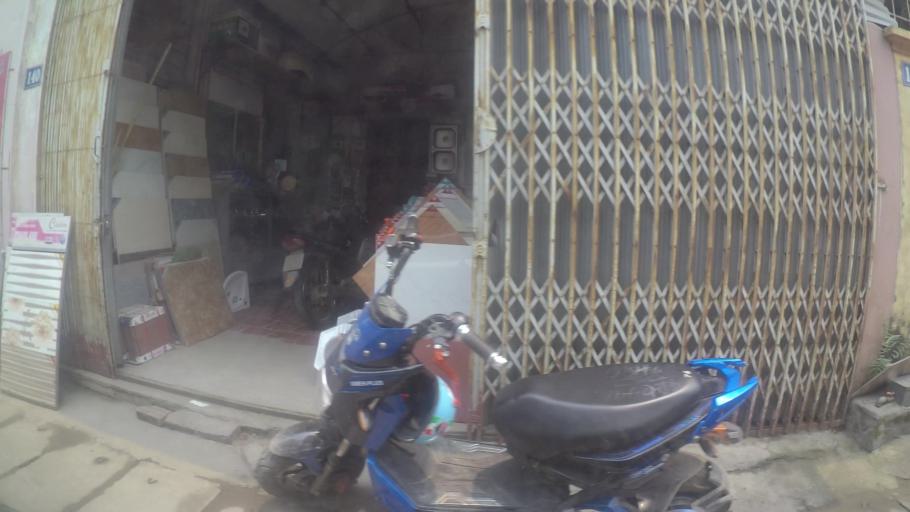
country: VN
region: Ha Noi
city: Ha Dong
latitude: 20.9826
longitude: 105.7488
